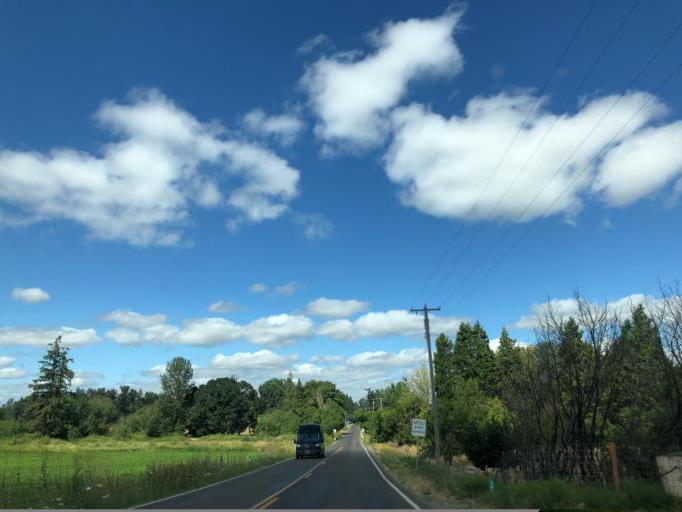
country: US
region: Oregon
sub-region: Marion County
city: Mount Angel
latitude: 45.1003
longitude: -122.7353
